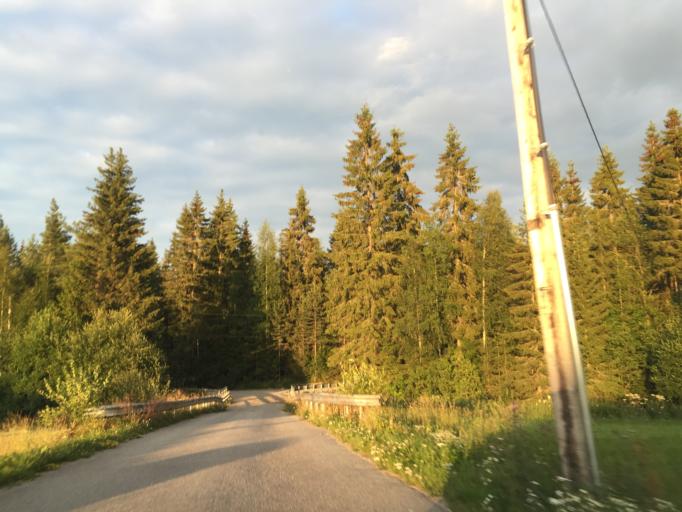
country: NO
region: Akershus
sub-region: Nes
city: Fjellfoten
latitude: 60.0901
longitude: 11.4906
